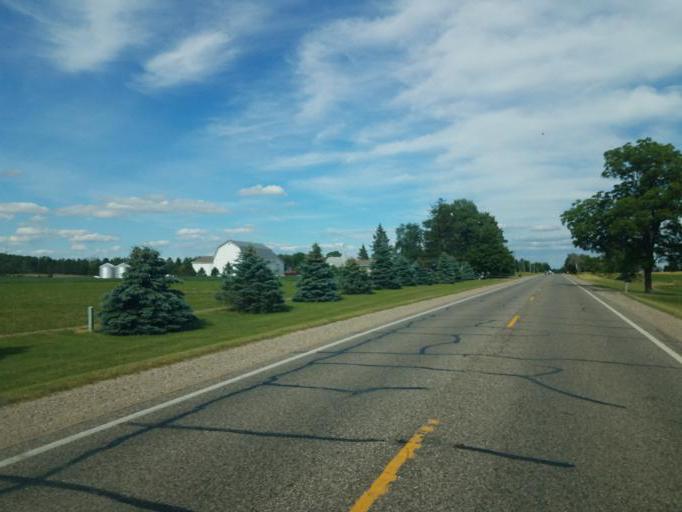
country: US
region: Michigan
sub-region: Eaton County
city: Charlotte
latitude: 42.5681
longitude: -84.8841
